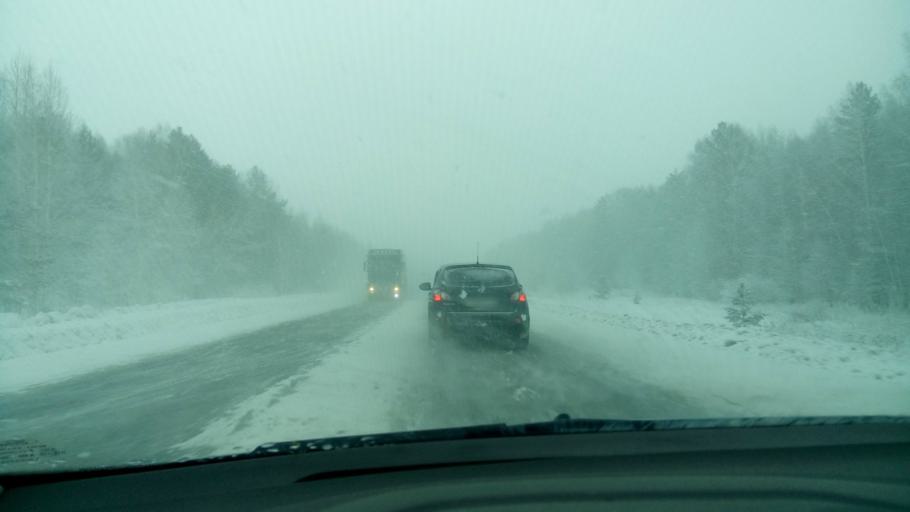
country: RU
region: Sverdlovsk
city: Beloyarskiy
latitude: 56.7723
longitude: 61.4910
